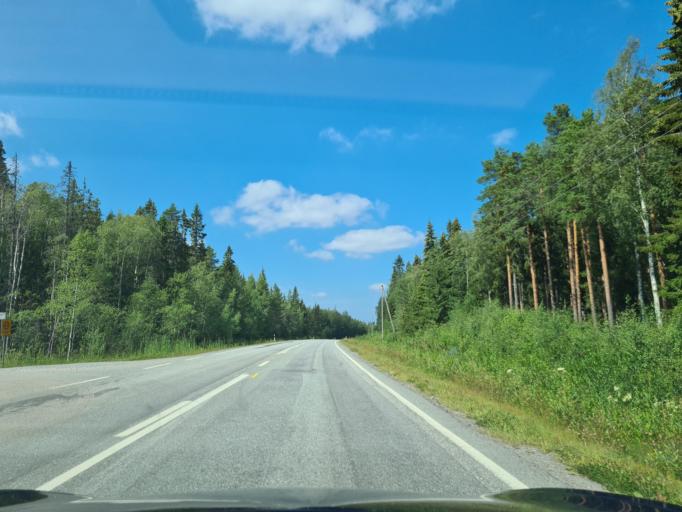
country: FI
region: Ostrobothnia
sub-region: Vaasa
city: Vaasa
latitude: 63.1823
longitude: 21.5703
